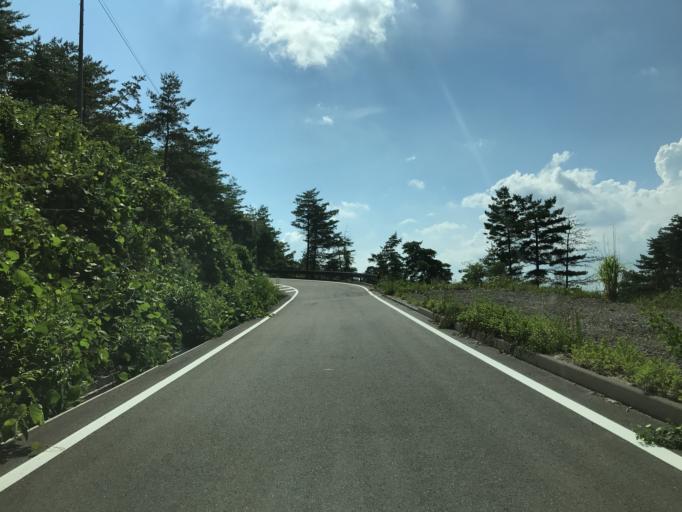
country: JP
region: Fukushima
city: Yanagawamachi-saiwaicho
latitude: 37.7835
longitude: 140.6680
